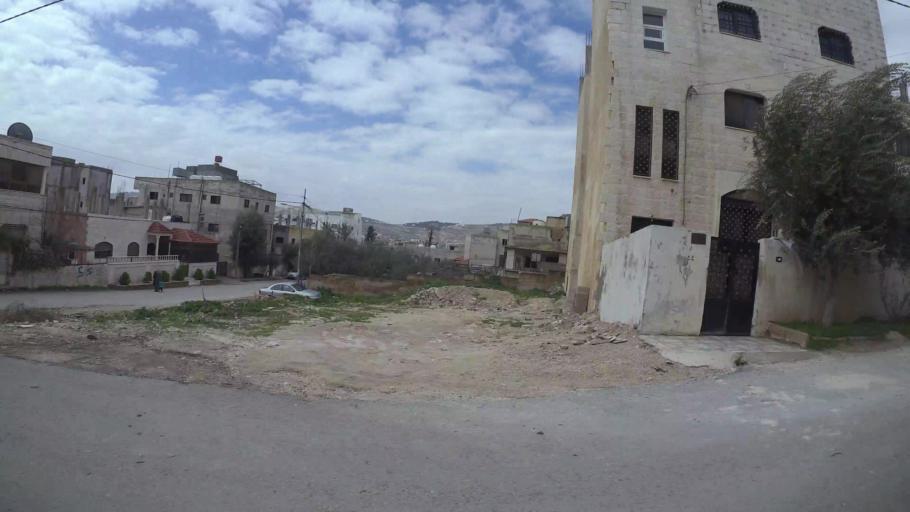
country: JO
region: Amman
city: Al Jubayhah
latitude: 32.0607
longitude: 35.8344
